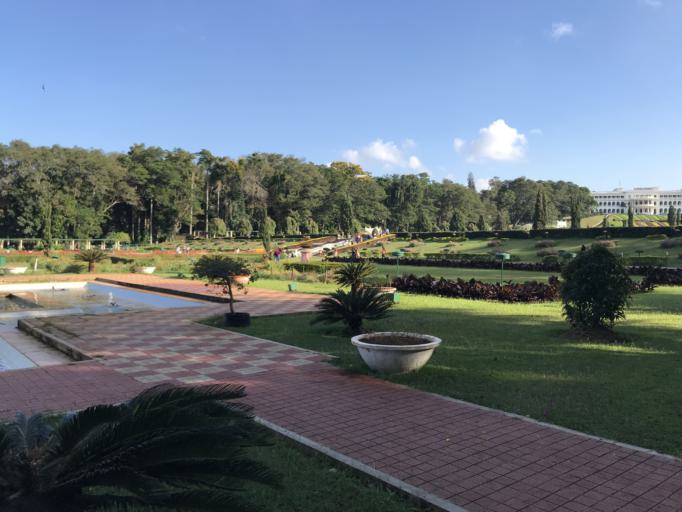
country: IN
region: Karnataka
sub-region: Mandya
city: Shrirangapattana
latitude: 12.4229
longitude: 76.5723
